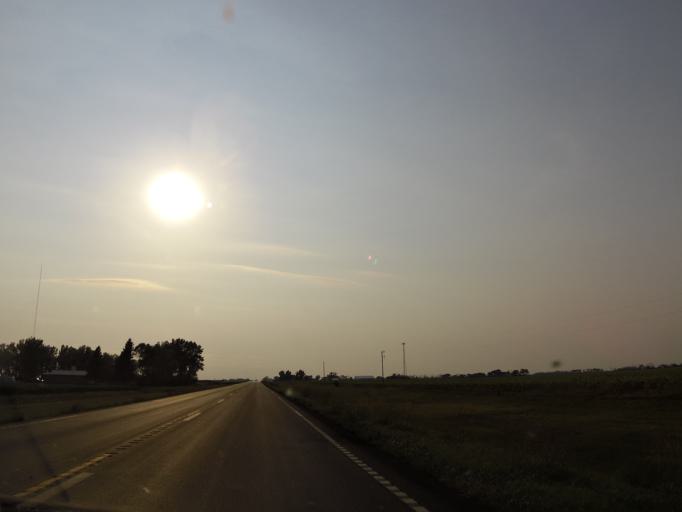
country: US
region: North Dakota
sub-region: Traill County
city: Mayville
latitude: 47.3529
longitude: -97.2535
